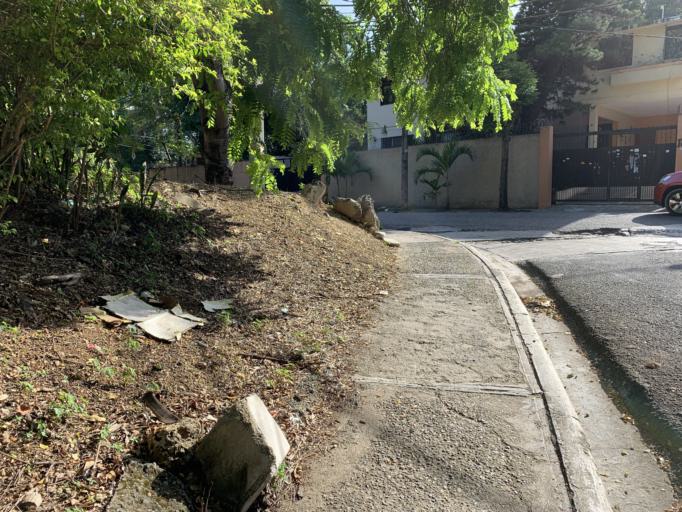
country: DO
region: Nacional
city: Santo Domingo
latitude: 18.4831
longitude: -69.9688
